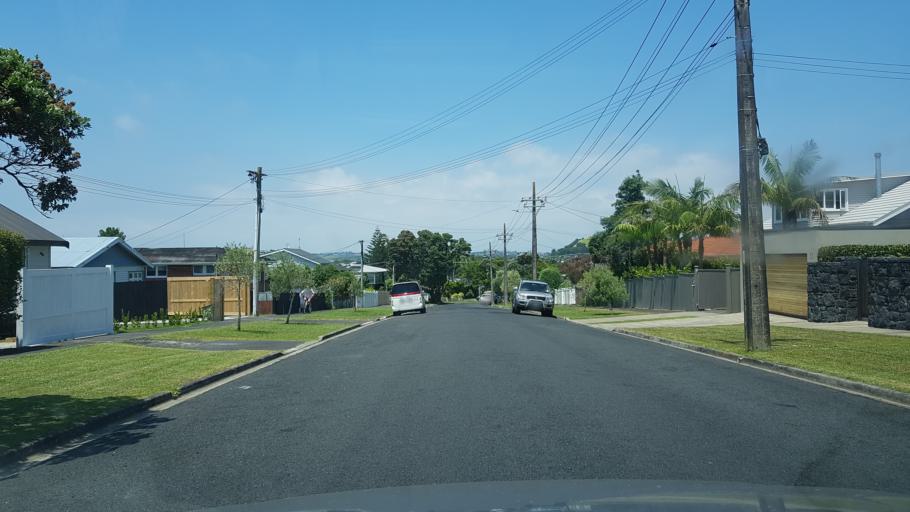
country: NZ
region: Auckland
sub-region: Auckland
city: North Shore
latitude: -36.8108
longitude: 174.7964
